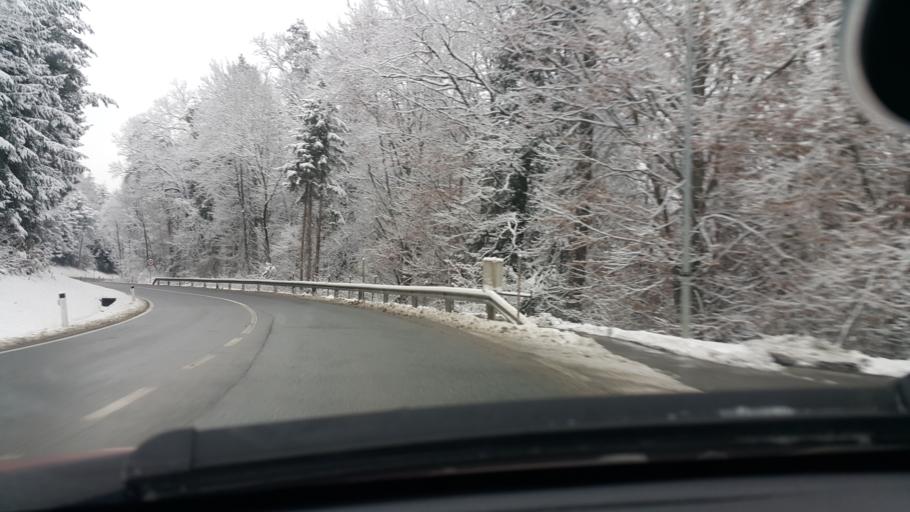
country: AT
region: Styria
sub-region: Politischer Bezirk Graz-Umgebung
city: Hitzendorf
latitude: 47.0248
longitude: 15.2985
